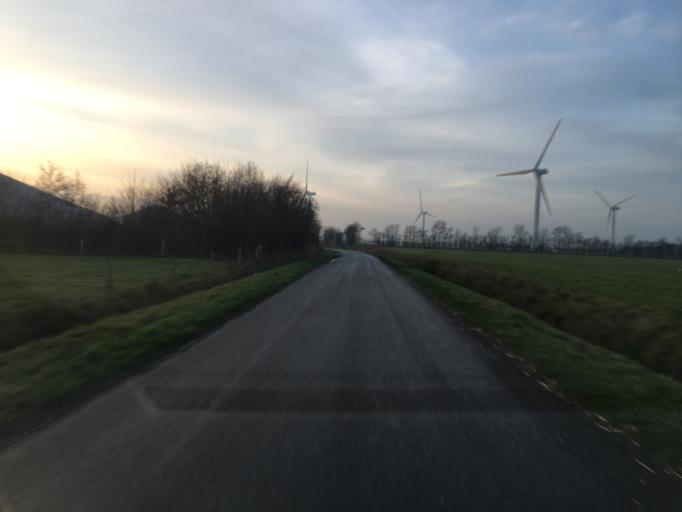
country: DK
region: South Denmark
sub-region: Tonder Kommune
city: Toftlund
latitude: 55.1169
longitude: 9.0309
